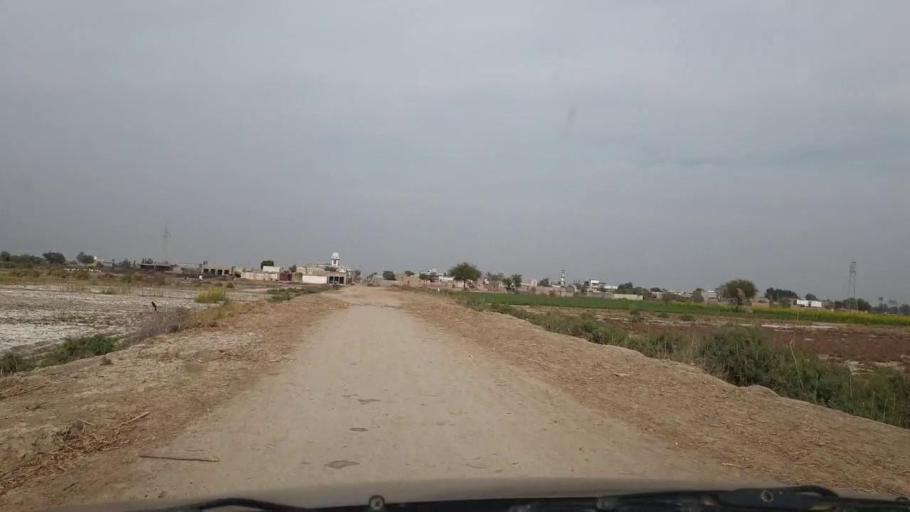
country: PK
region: Sindh
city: Sinjhoro
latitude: 26.1005
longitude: 68.8274
